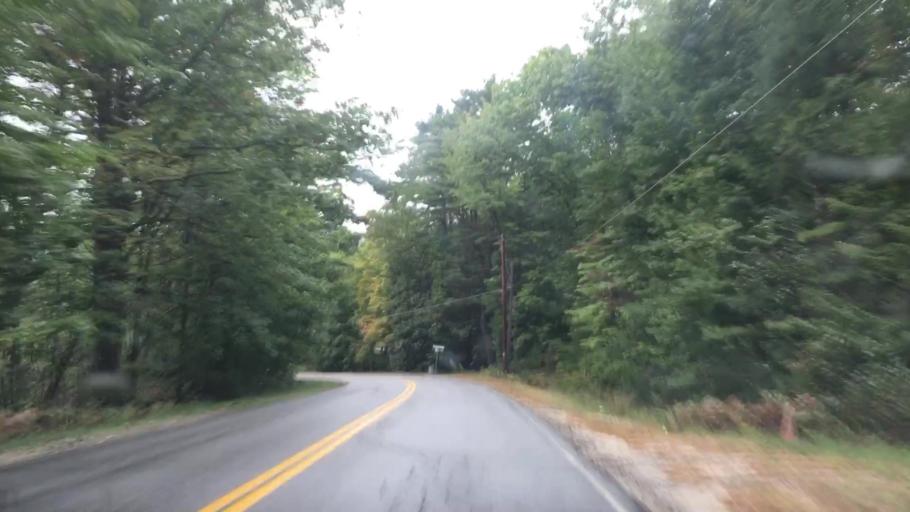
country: US
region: Maine
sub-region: Cumberland County
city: Raymond
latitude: 43.9386
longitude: -70.4276
